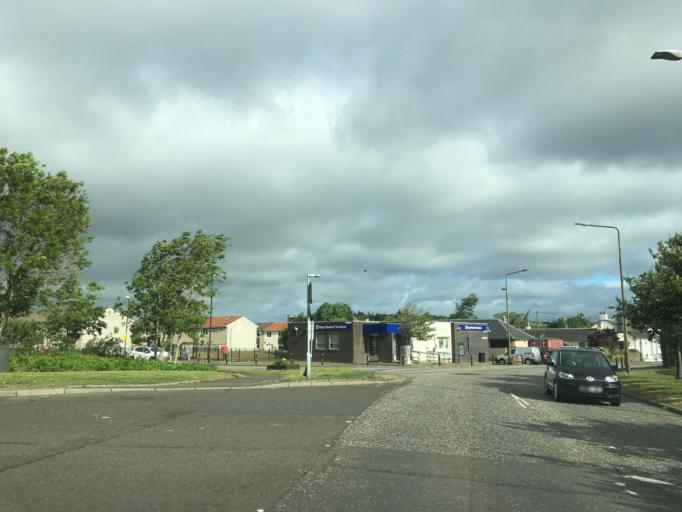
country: GB
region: Scotland
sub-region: Edinburgh
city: Newbridge
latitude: 55.9379
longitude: -3.4076
